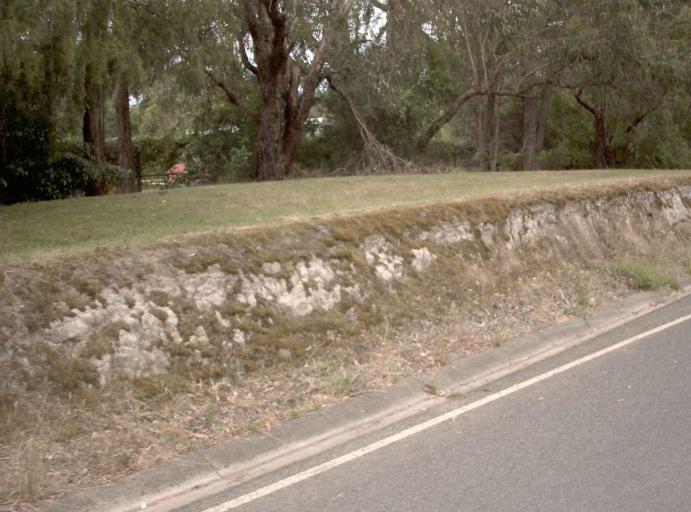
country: AU
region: Victoria
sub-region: Yarra Ranges
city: Mount Evelyn
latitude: -37.7595
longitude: 145.3924
